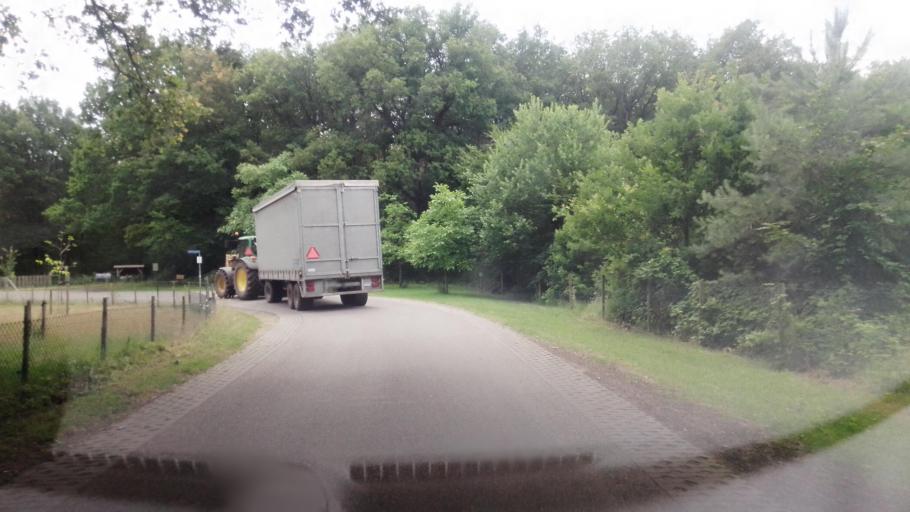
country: NL
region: Limburg
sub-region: Gemeente Peel en Maas
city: Maasbree
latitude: 51.4059
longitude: 5.9999
